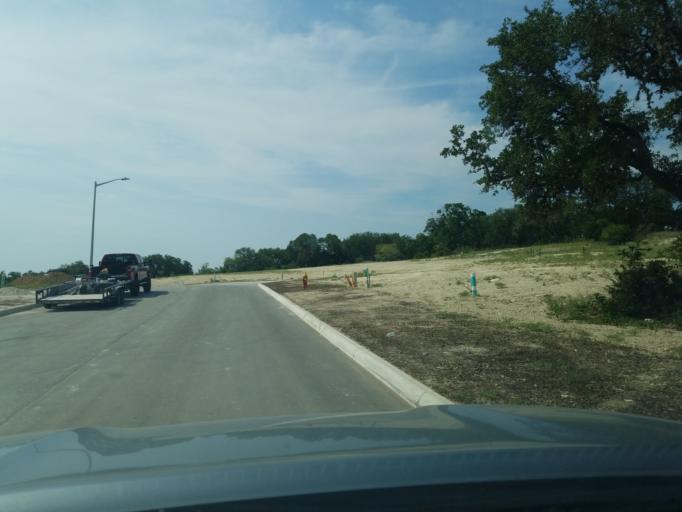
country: US
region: Texas
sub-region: Kendall County
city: Boerne
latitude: 29.7513
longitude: -98.7172
